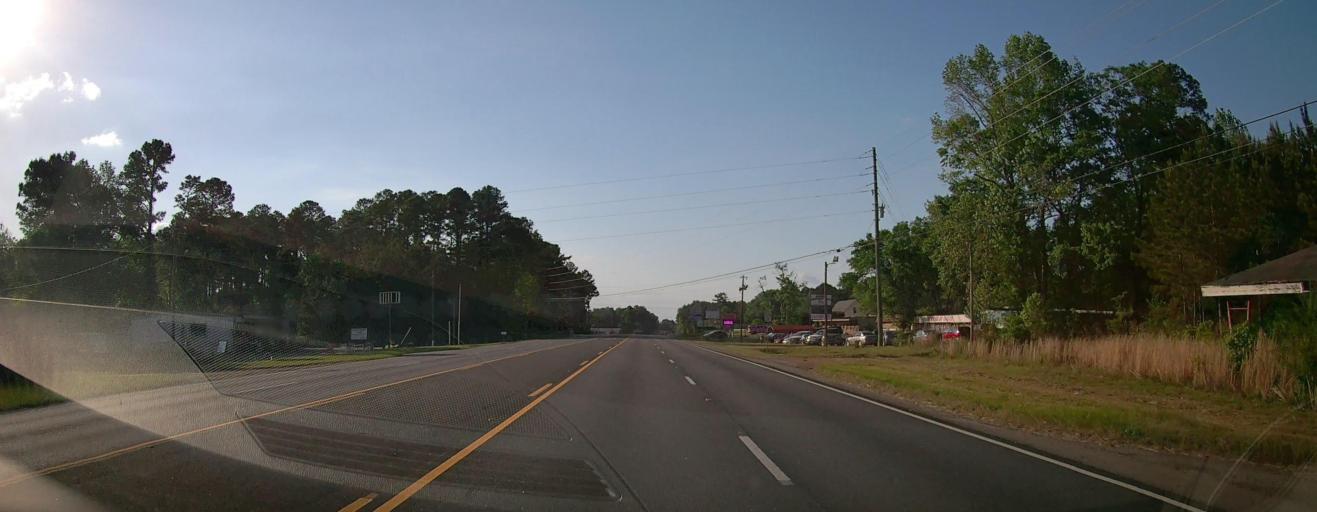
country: US
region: Georgia
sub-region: Baldwin County
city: Milledgeville
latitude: 33.1758
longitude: -83.2847
